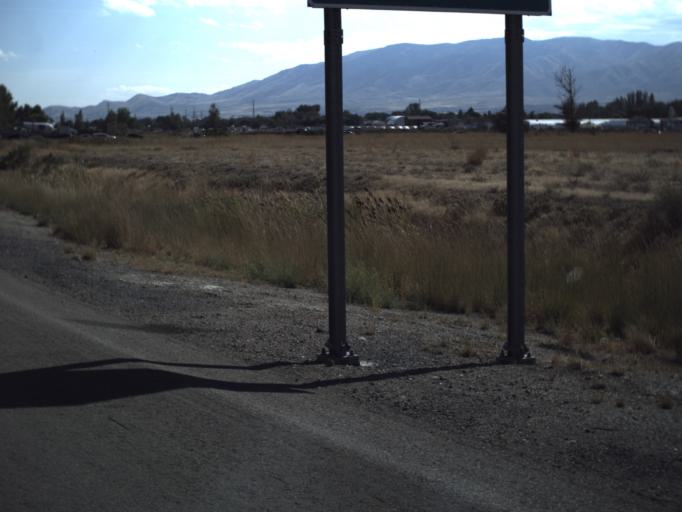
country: US
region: Utah
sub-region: Utah County
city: Lehi
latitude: 40.4152
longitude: -111.8732
